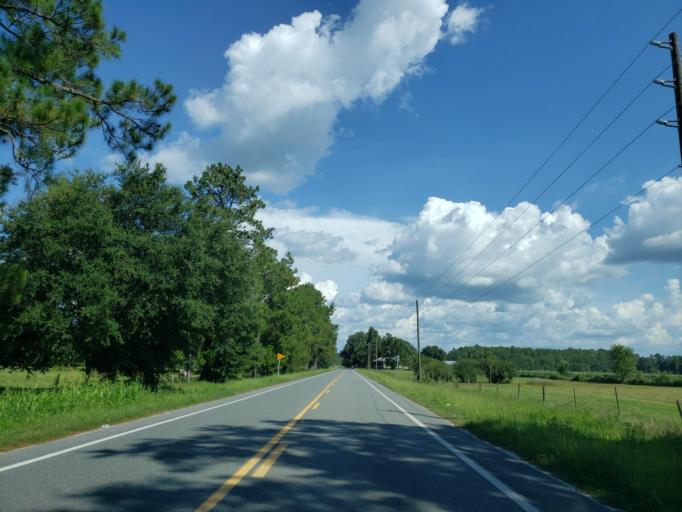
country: US
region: Georgia
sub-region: Echols County
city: Statenville
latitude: 30.5729
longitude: -83.1639
